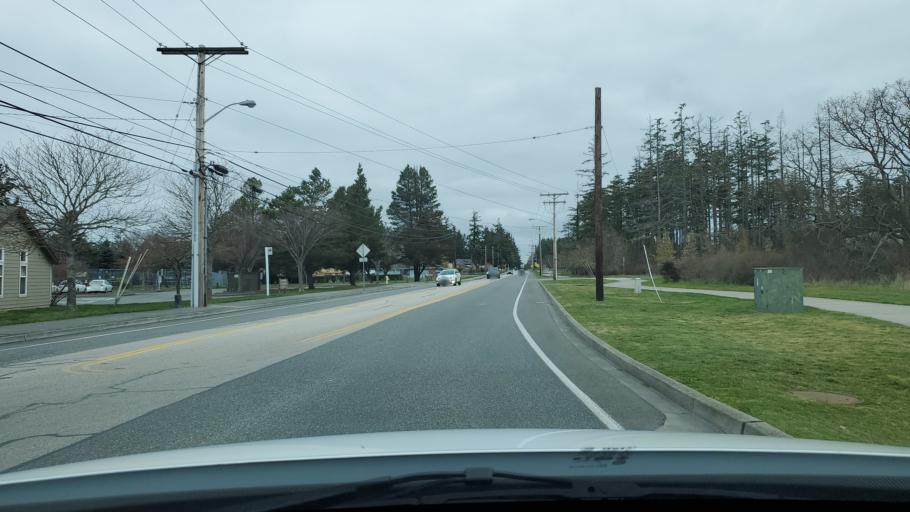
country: US
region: Washington
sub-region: Island County
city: Oak Harbor
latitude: 48.2980
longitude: -122.6356
